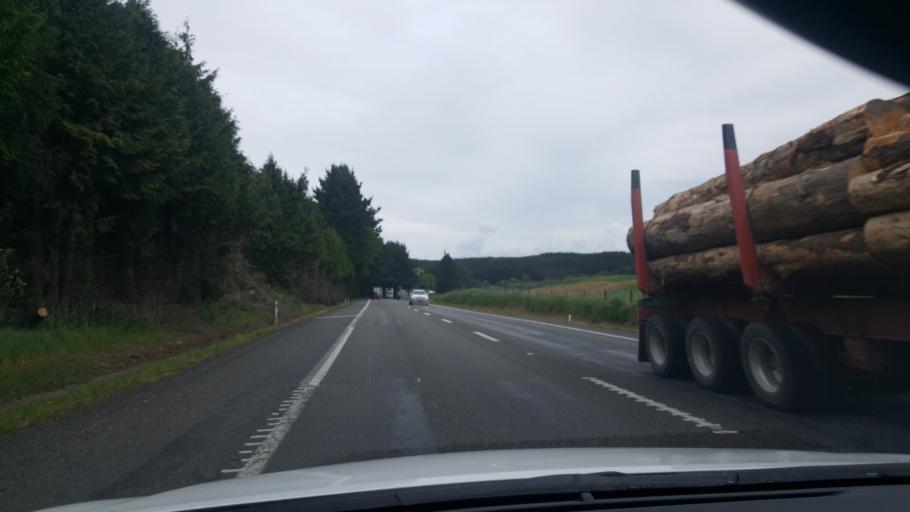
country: NZ
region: Bay of Plenty
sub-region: Rotorua District
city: Rotorua
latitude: -38.2714
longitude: 176.3344
